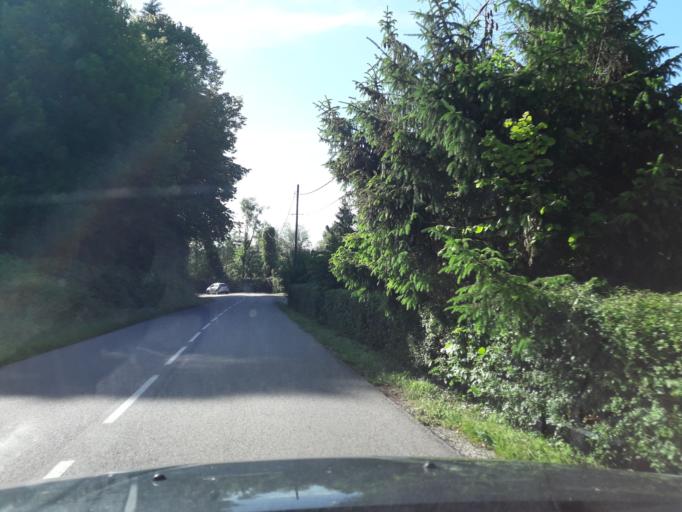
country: FR
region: Rhone-Alpes
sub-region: Departement de la Savoie
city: Vimines
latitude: 45.5409
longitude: 5.8055
